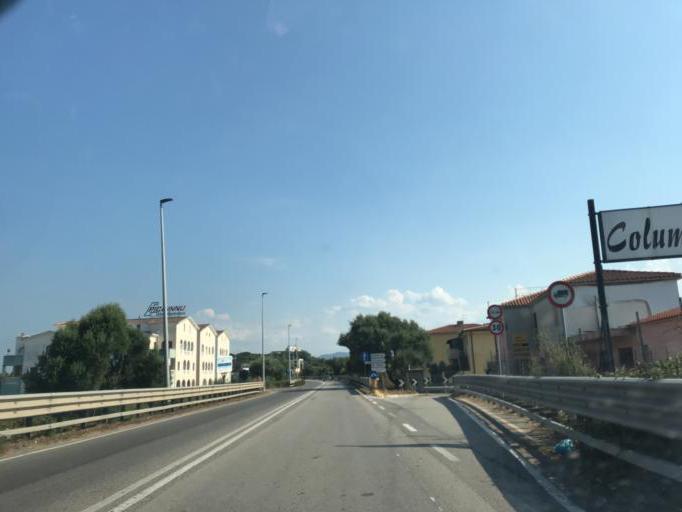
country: IT
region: Sardinia
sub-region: Provincia di Olbia-Tempio
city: Olbia
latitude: 40.9156
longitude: 9.5016
